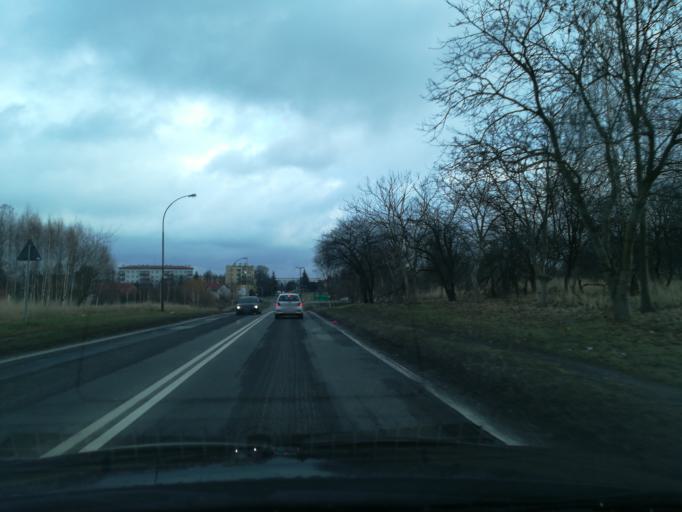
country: PL
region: Subcarpathian Voivodeship
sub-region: Powiat lancucki
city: Lancut
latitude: 50.0623
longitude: 22.2244
